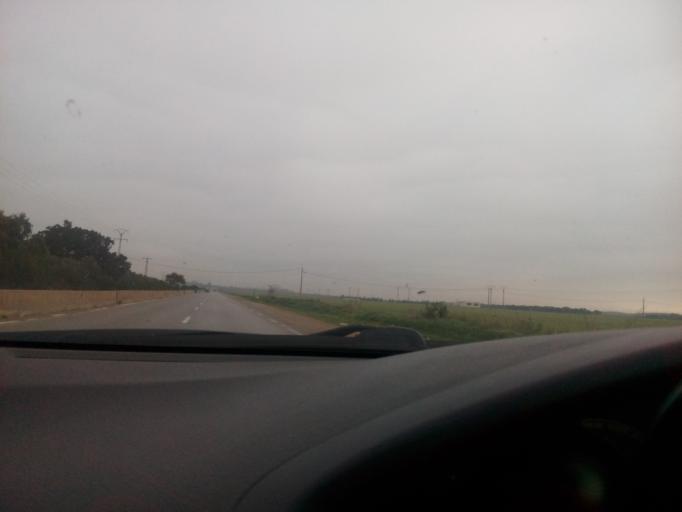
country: DZ
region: Oran
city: Bou Tlelis
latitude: 35.5507
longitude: -0.9538
